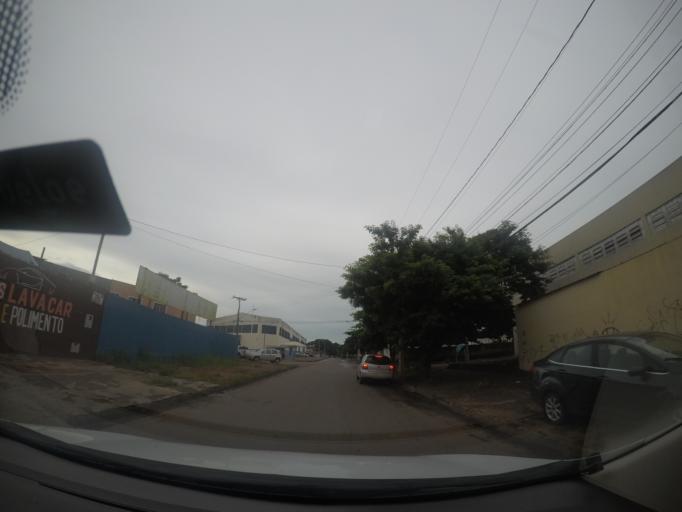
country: BR
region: Goias
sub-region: Goiania
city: Goiania
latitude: -16.6353
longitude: -49.2386
